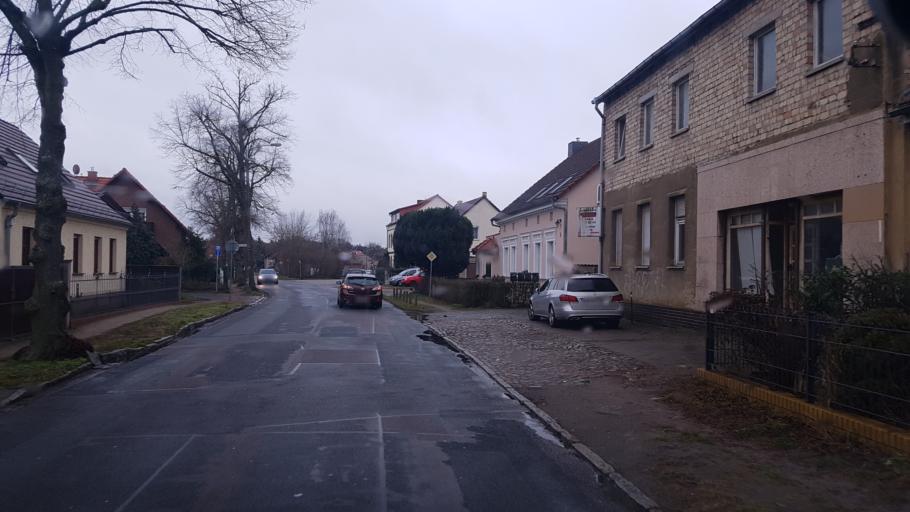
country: DE
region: Berlin
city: Wannsee
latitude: 52.3611
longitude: 13.1268
